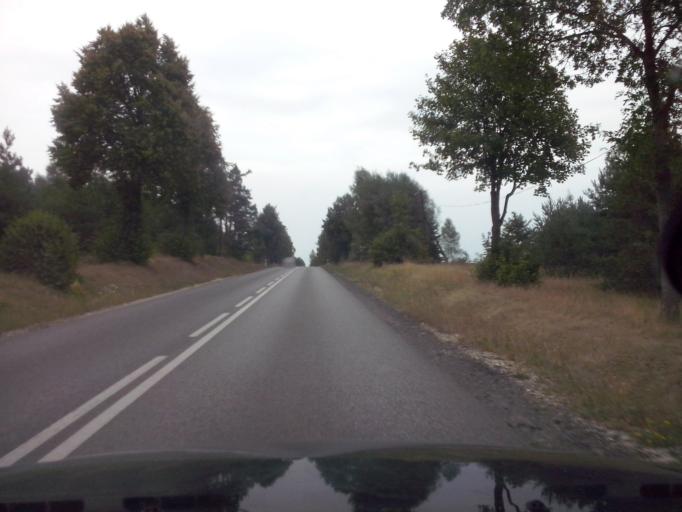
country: PL
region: Swietokrzyskie
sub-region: Powiat kielecki
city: Morawica
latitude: 50.7053
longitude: 20.6026
